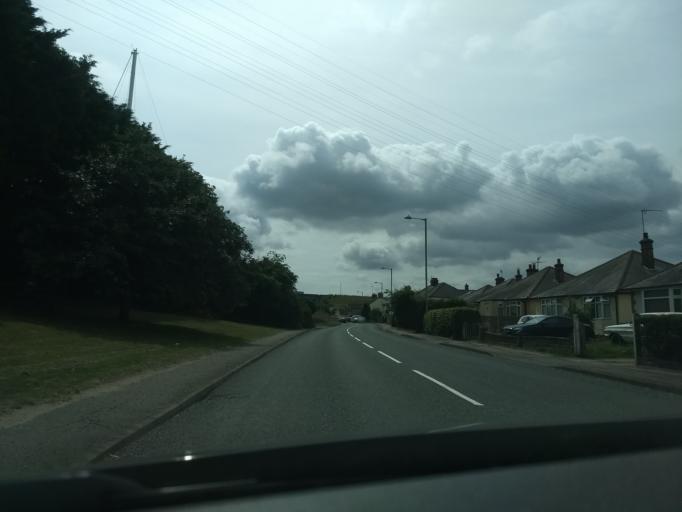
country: GB
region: England
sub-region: Suffolk
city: Ipswich
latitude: 52.0323
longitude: 1.1526
